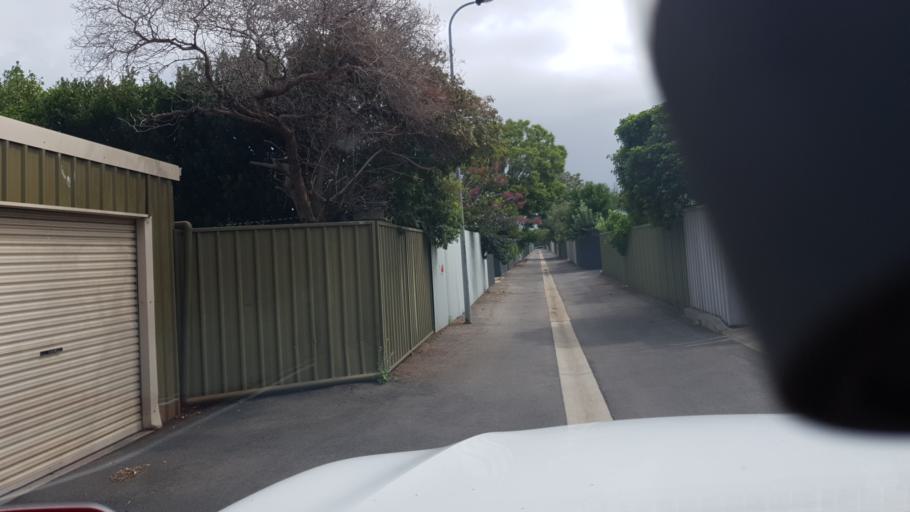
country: AU
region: South Australia
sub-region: Adelaide
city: Brighton
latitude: -35.0227
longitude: 138.5249
